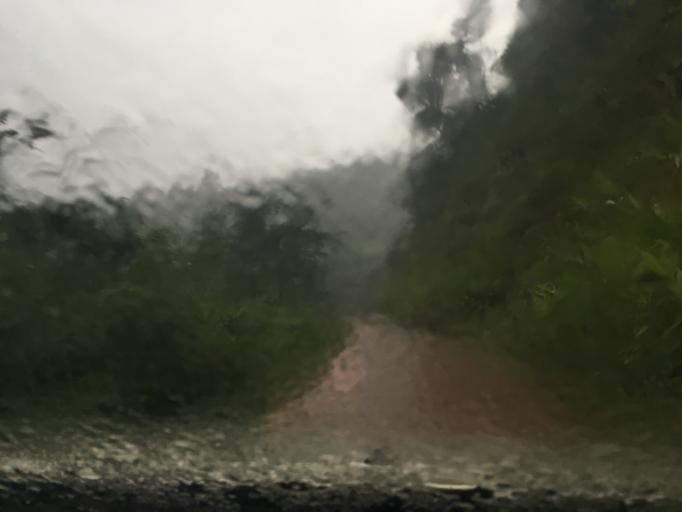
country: LA
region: Oudomxai
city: Muang La
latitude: 21.2303
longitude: 101.9617
